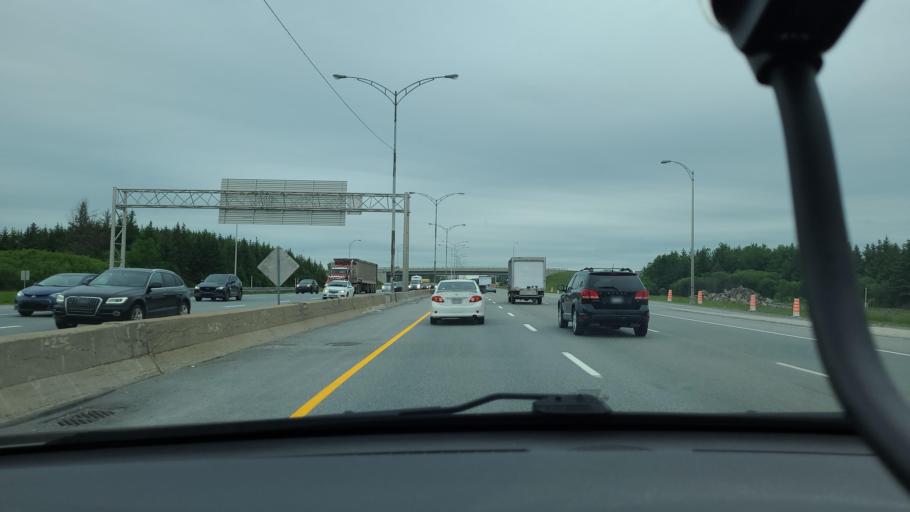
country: CA
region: Quebec
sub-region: Laval
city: Laval
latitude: 45.6266
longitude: -73.6599
